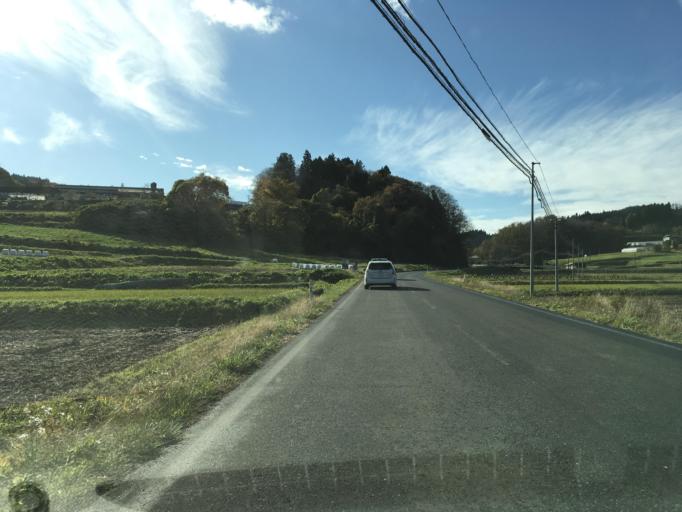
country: JP
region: Iwate
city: Ichinoseki
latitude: 38.9214
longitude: 141.4206
